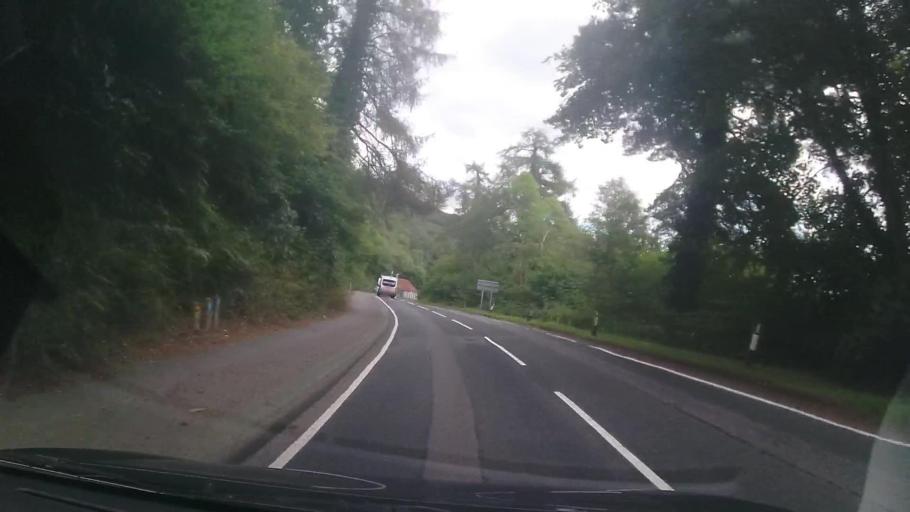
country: GB
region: Scotland
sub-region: Highland
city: Fort William
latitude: 56.7027
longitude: -5.2089
